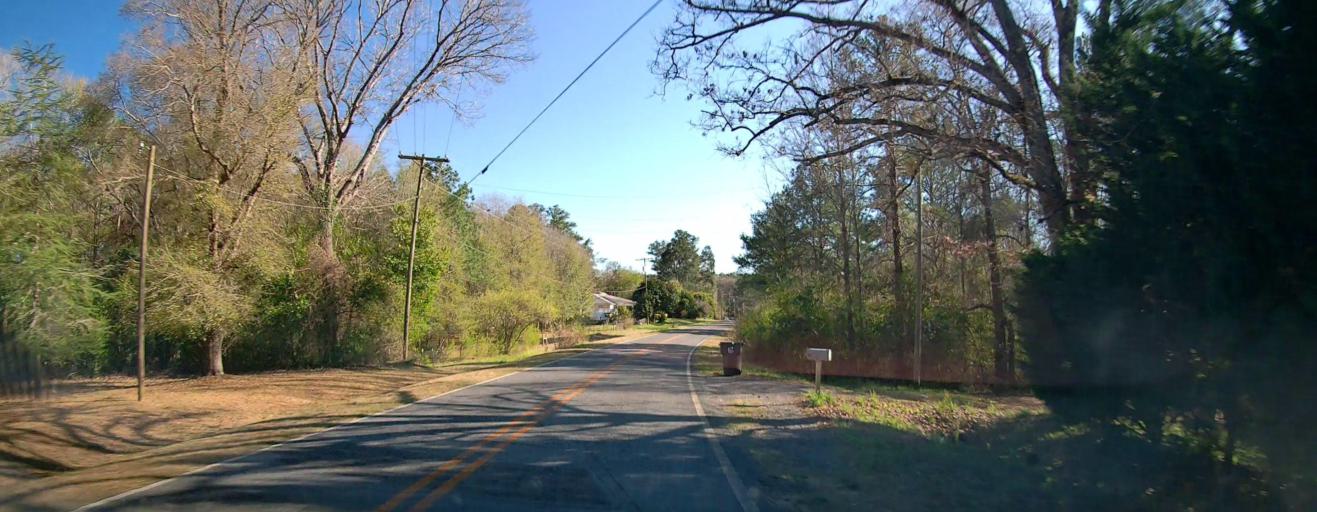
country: US
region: Georgia
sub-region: Peach County
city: Fort Valley
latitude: 32.5887
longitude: -83.8514
